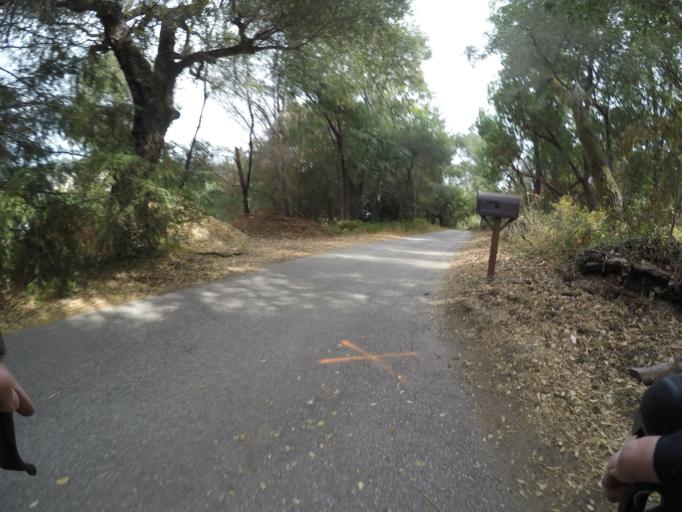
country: US
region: California
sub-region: Santa Cruz County
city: Mount Hermon
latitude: 37.0666
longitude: -122.0615
